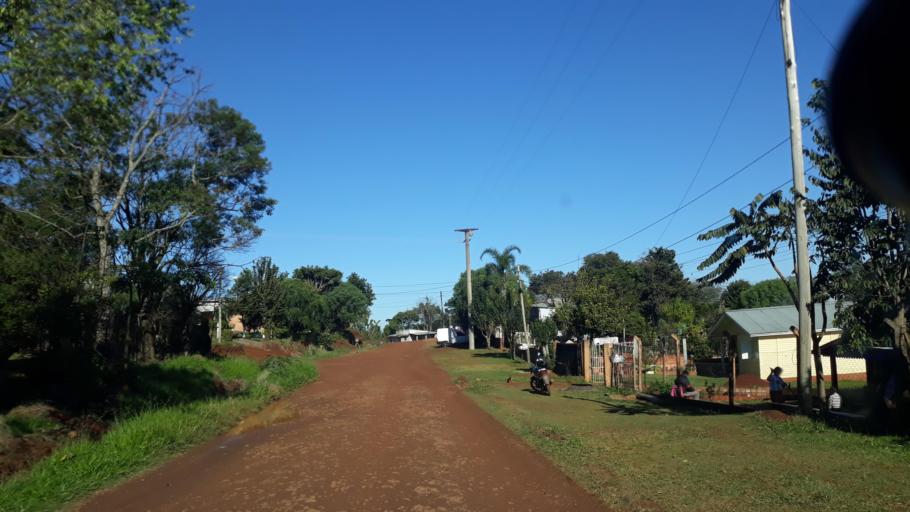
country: AR
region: Misiones
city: Bernardo de Irigoyen
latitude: -26.2648
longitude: -53.6591
